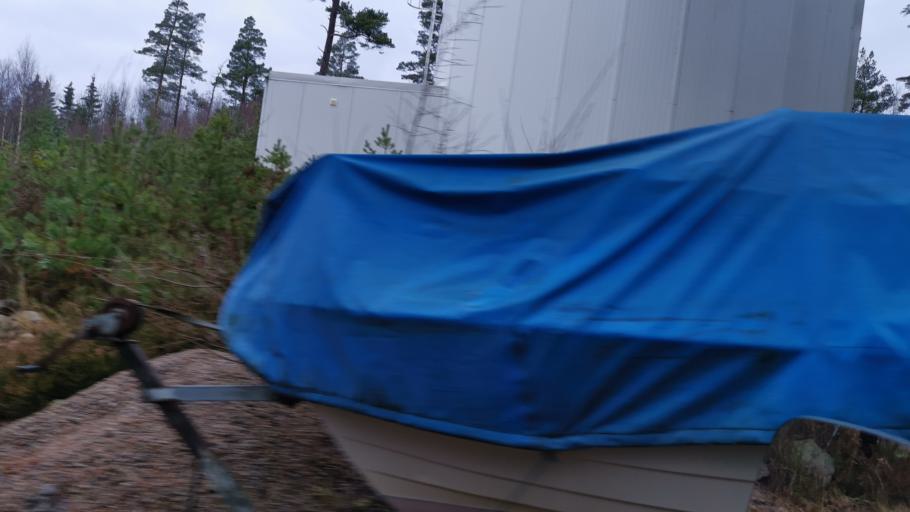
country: SE
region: Vaestra Goetaland
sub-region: Orust
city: Henan
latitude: 58.3410
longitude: 11.7201
